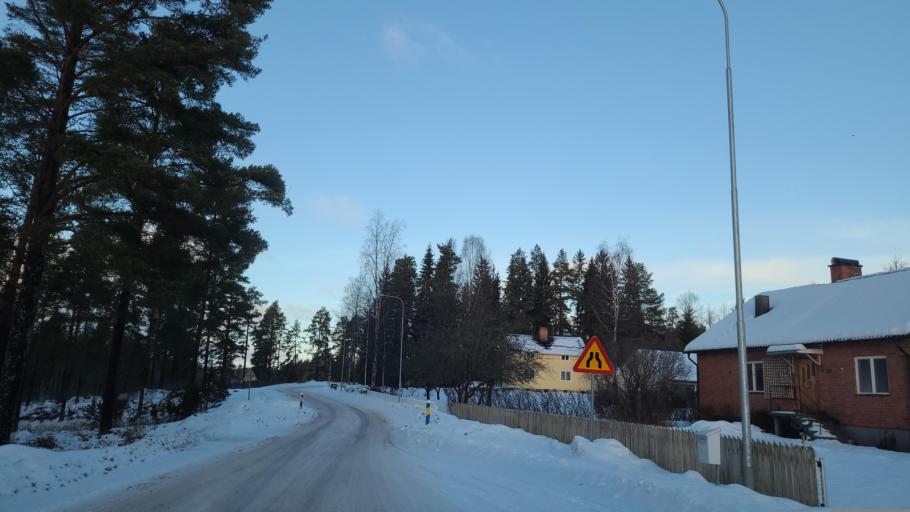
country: SE
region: Gaevleborg
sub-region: Bollnas Kommun
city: Bollnas
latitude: 61.3714
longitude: 16.3993
